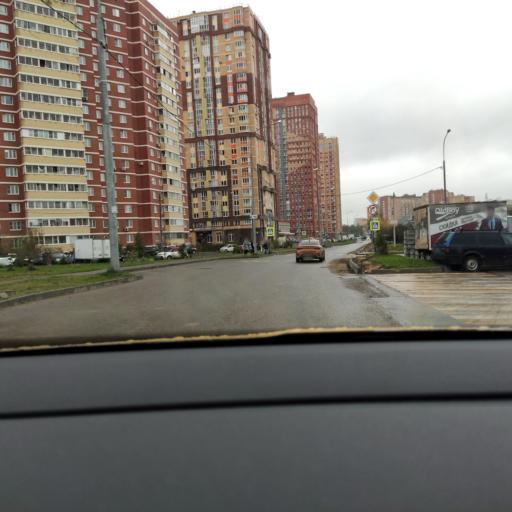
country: RU
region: Moskovskaya
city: Shcherbinka
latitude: 55.5042
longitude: 37.5330
